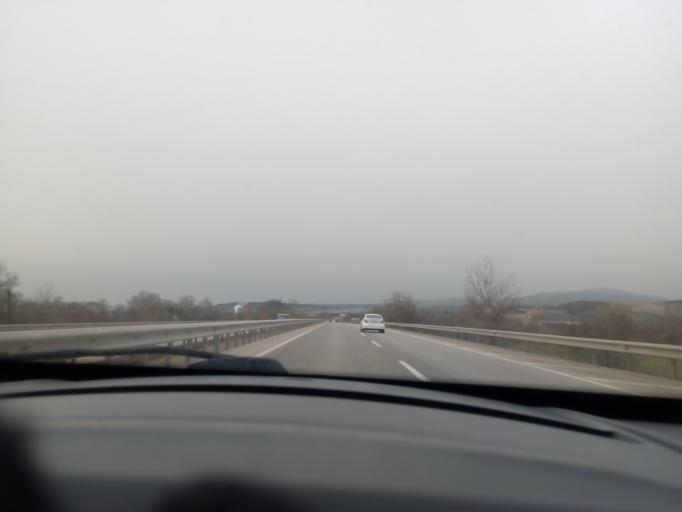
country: TR
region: Balikesir
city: Gobel
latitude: 39.9800
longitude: 28.1856
